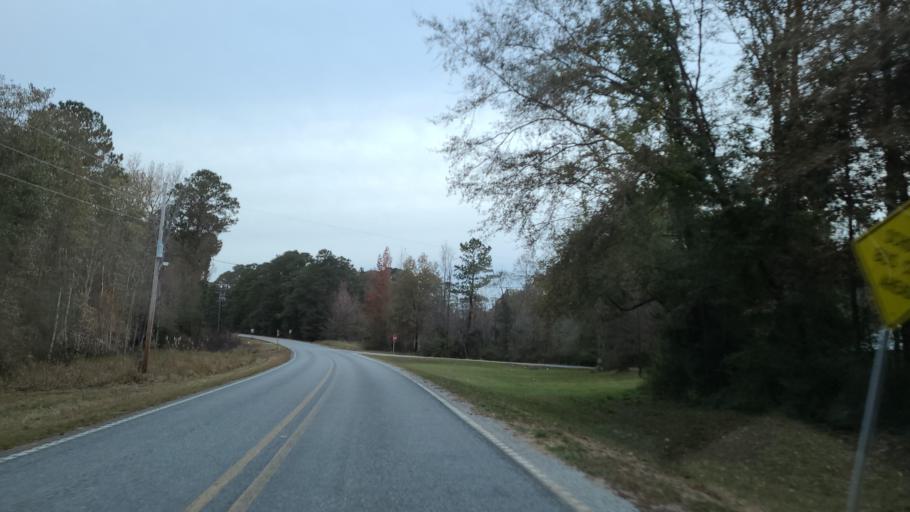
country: US
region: Mississippi
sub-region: Clarke County
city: Stonewall
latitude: 32.0222
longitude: -88.8513
